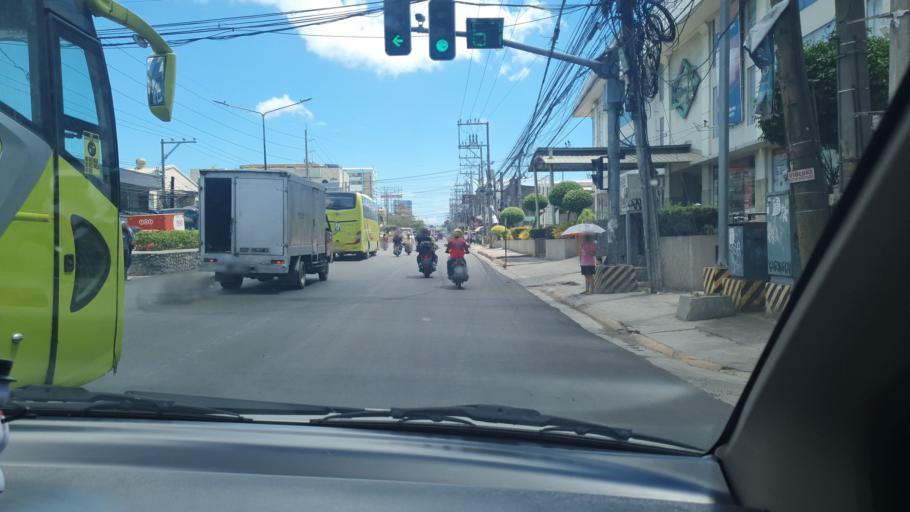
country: PH
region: Central Visayas
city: Mandaue City
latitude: 10.3320
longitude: 123.9355
